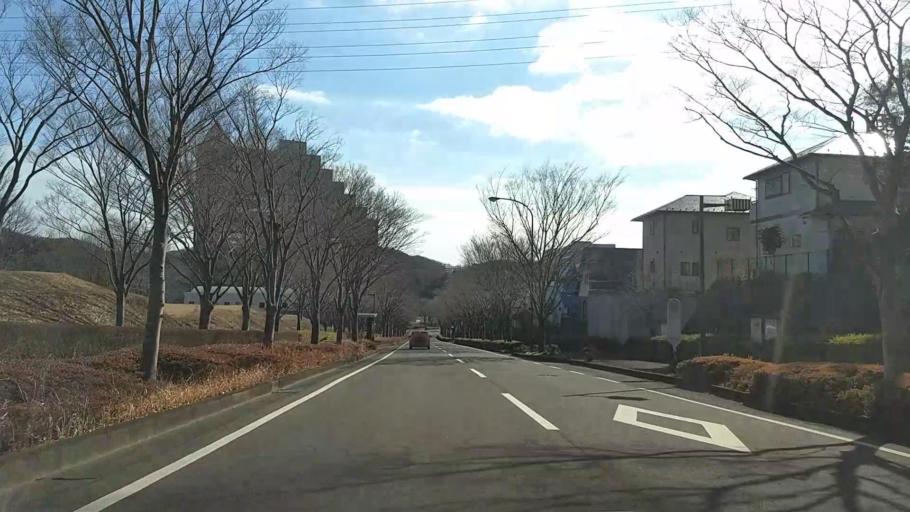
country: JP
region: Kanagawa
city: Atsugi
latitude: 35.4509
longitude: 139.3081
